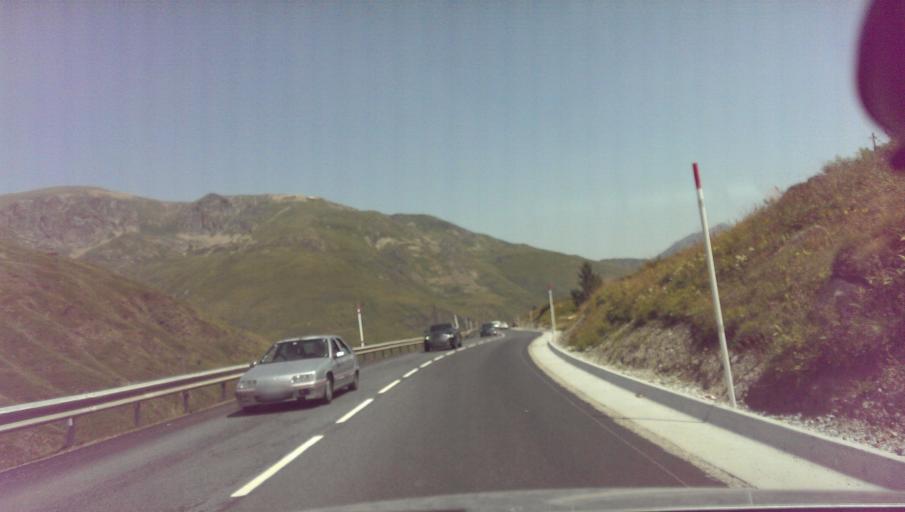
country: AD
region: Encamp
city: Pas de la Casa
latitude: 42.5524
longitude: 1.7398
